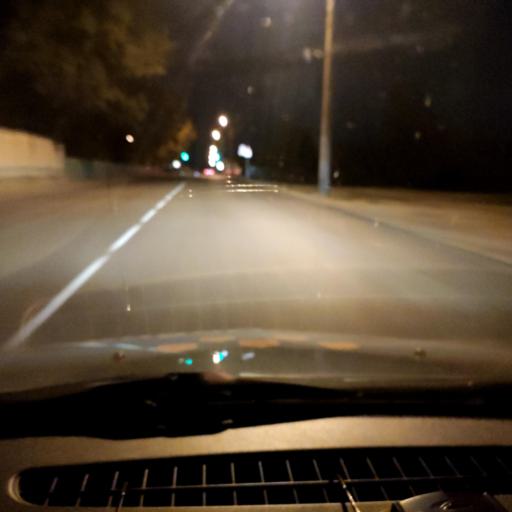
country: RU
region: Voronezj
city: Voronezh
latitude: 51.6300
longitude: 39.1752
